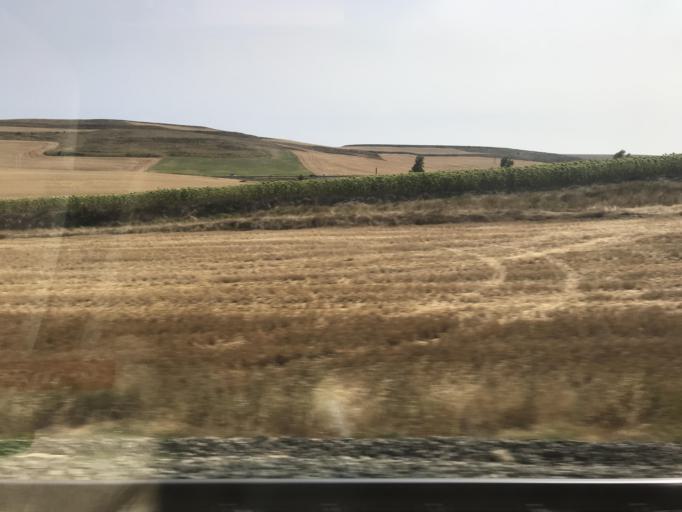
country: ES
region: Castille and Leon
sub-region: Provincia de Burgos
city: Villanueva de Teba
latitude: 42.6260
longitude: -3.1431
